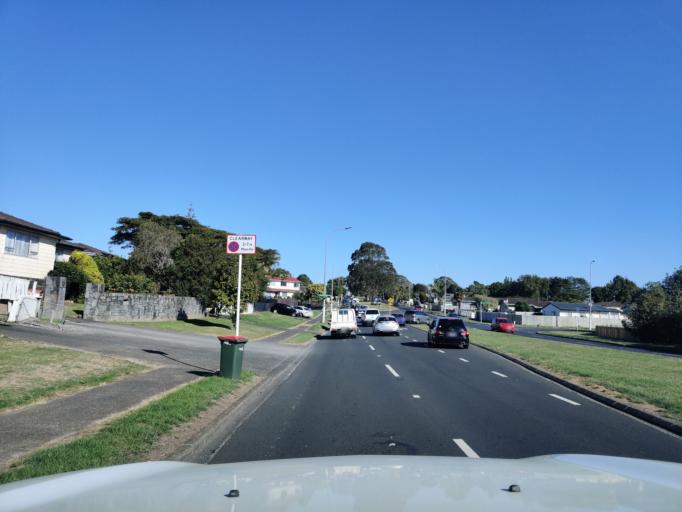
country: NZ
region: Auckland
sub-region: Auckland
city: Wiri
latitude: -37.0206
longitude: 174.8632
